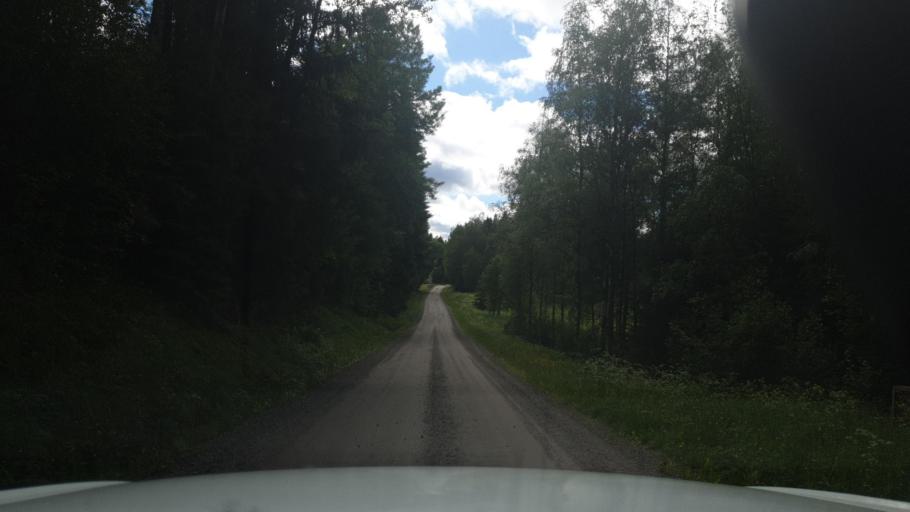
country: NO
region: Ostfold
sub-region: Romskog
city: Romskog
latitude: 59.7051
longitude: 11.9587
